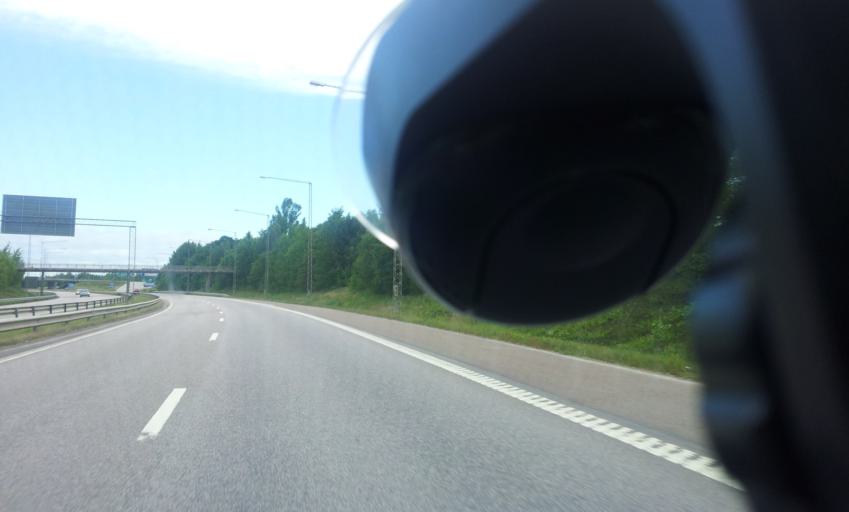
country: SE
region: Kalmar
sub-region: Kalmar Kommun
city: Kalmar
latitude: 56.6782
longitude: 16.3284
